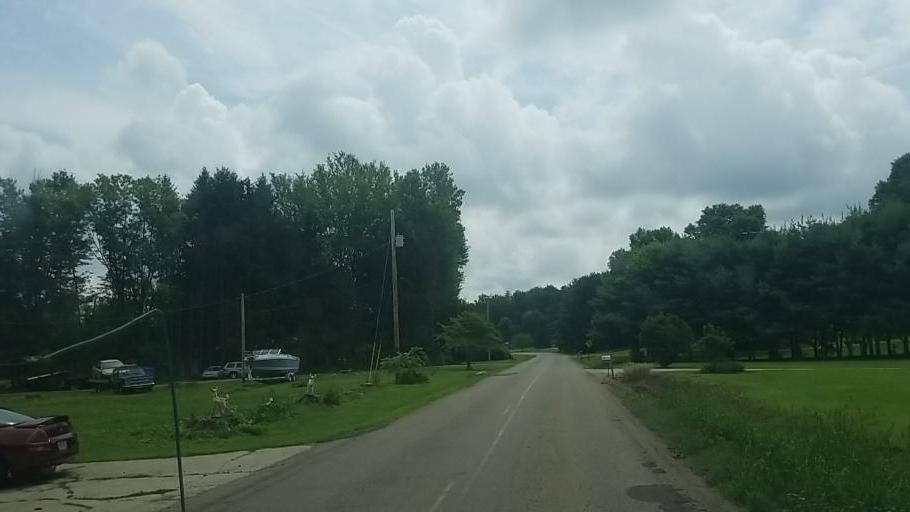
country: US
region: Ohio
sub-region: Knox County
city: Gambier
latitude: 40.3967
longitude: -82.3660
